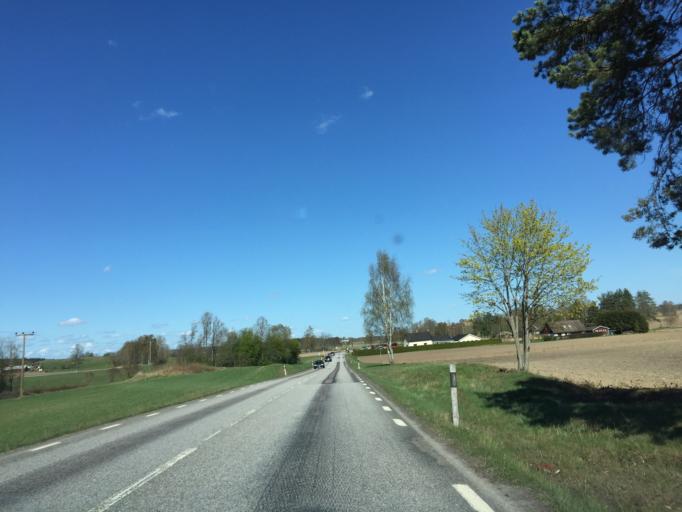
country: SE
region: OErebro
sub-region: Hallsbergs Kommun
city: Skollersta
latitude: 59.1083
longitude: 15.3266
